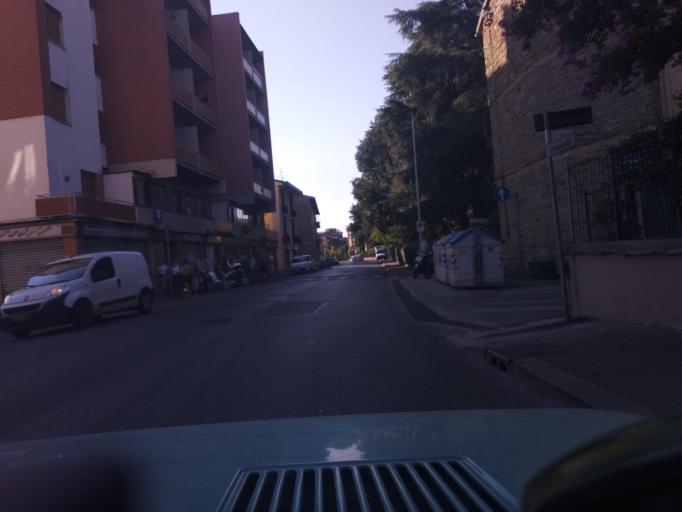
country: IT
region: Tuscany
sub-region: Province of Florence
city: Florence
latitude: 43.7770
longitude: 11.2149
